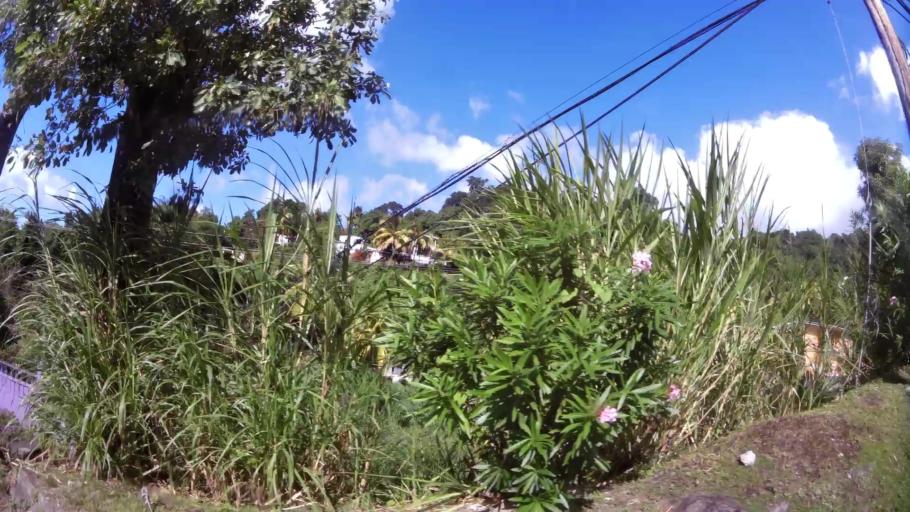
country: DM
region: Saint Luke
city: Pointe Michel
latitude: 15.2756
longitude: -61.3729
